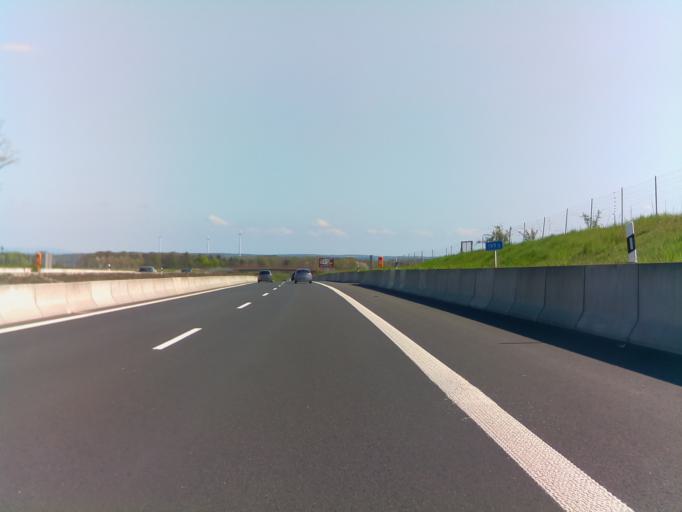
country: DE
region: Bavaria
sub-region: Regierungsbezirk Unterfranken
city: Rannungen
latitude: 50.1768
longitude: 10.1926
